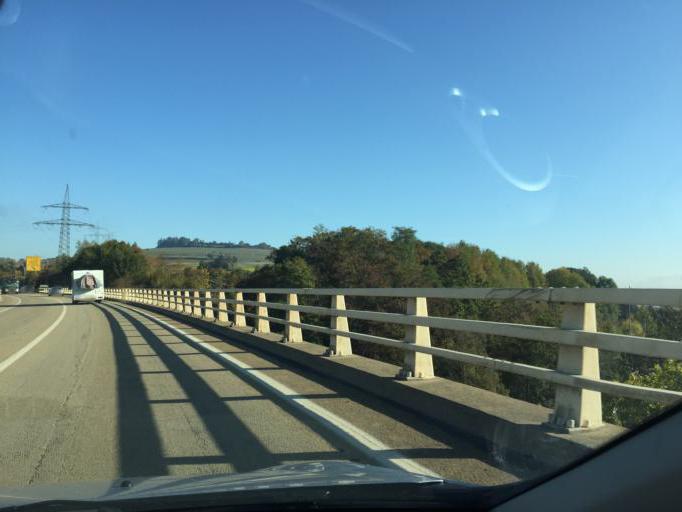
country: LU
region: Diekirch
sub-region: Canton de Diekirch
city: Erpeldange
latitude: 49.8501
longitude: 6.1211
